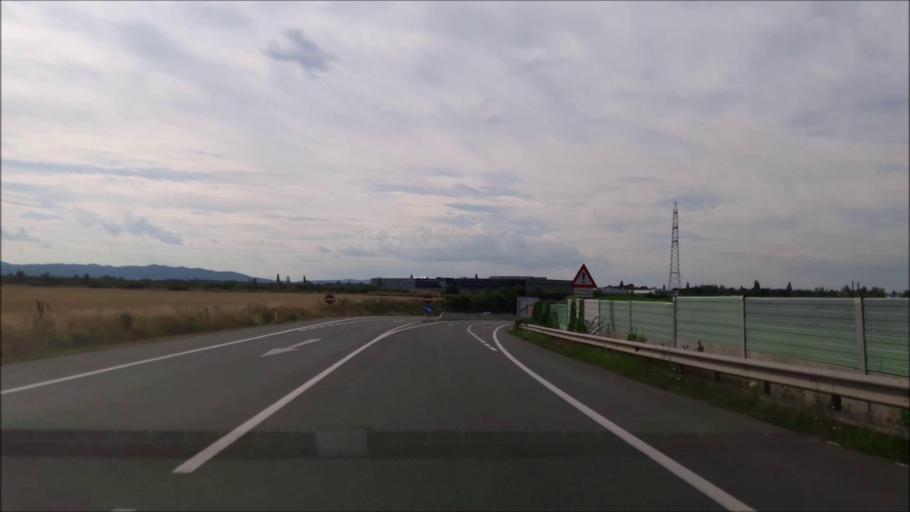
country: AT
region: Lower Austria
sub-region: Politischer Bezirk Modling
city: Achau
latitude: 48.0949
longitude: 16.4034
